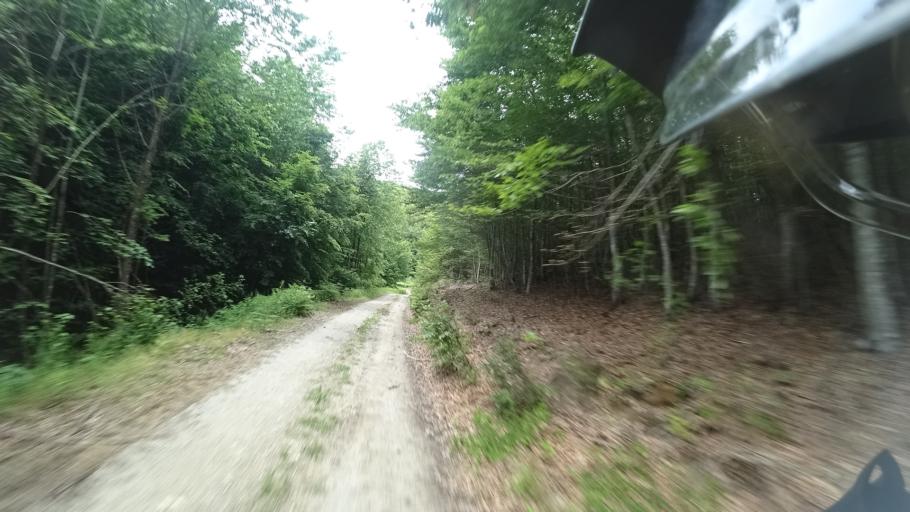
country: HR
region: Karlovacka
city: Vojnic
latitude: 45.2419
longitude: 15.6844
